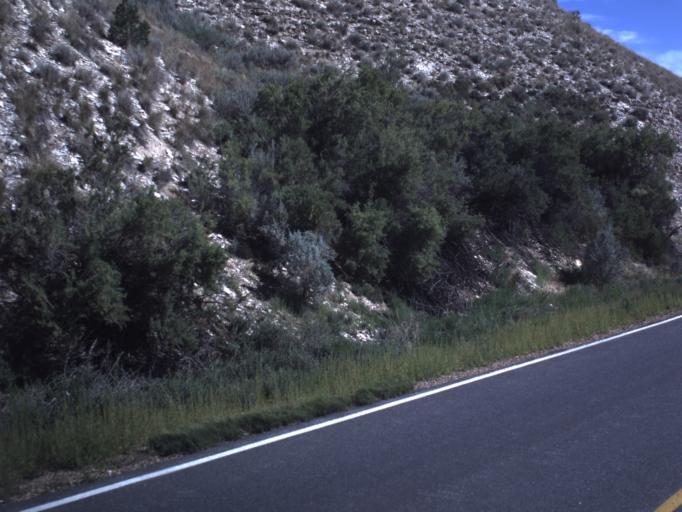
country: US
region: Utah
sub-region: Duchesne County
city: Duchesne
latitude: 40.0664
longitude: -110.5143
